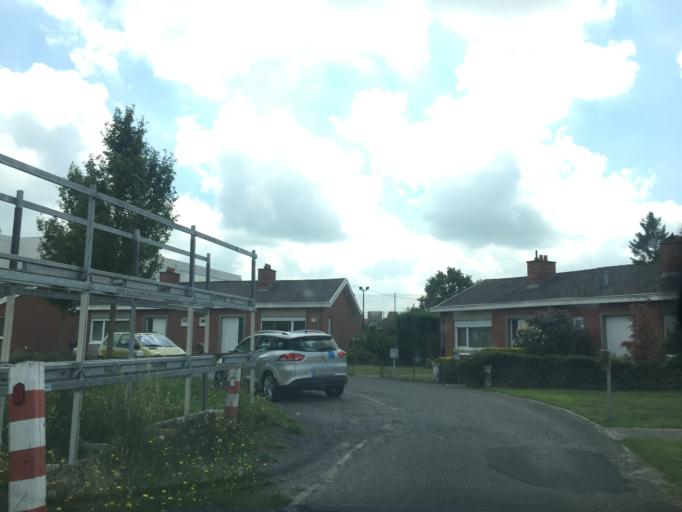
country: BE
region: Flanders
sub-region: Provincie West-Vlaanderen
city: Kortemark
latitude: 51.0305
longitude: 3.0371
